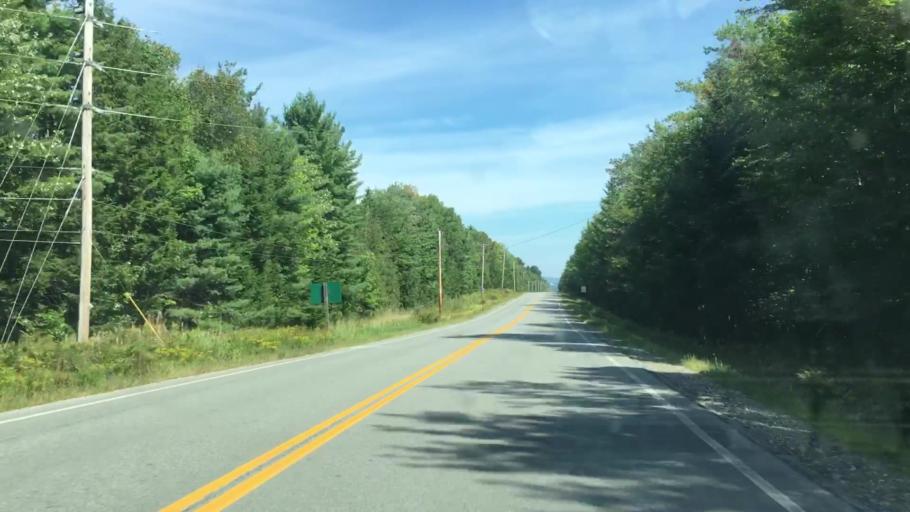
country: US
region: Maine
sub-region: Penobscot County
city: Howland
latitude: 45.2304
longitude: -68.7718
